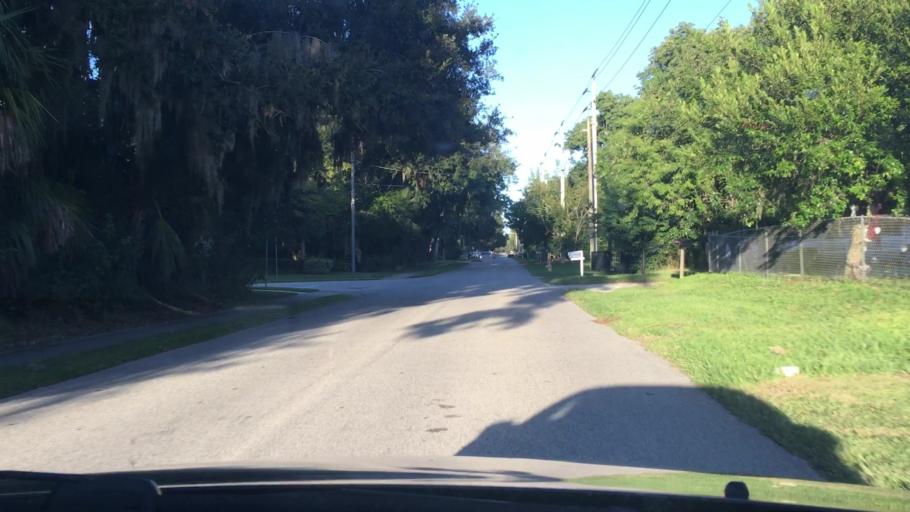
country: US
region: Florida
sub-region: Volusia County
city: Holly Hill
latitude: 29.2367
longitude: -81.0537
